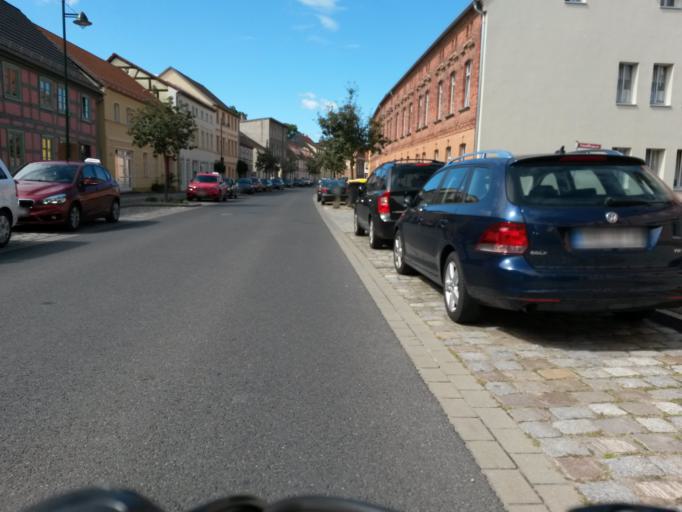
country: DE
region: Brandenburg
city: Angermunde
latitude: 53.0160
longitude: 14.0030
